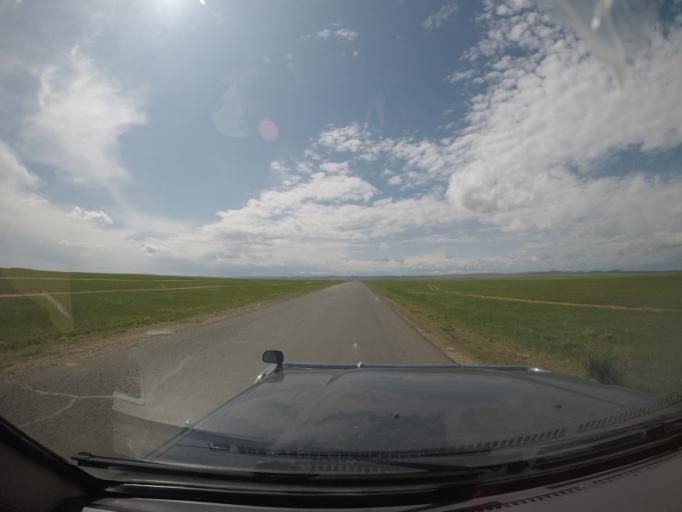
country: MN
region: Hentiy
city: Moron
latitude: 47.4209
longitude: 110.0501
